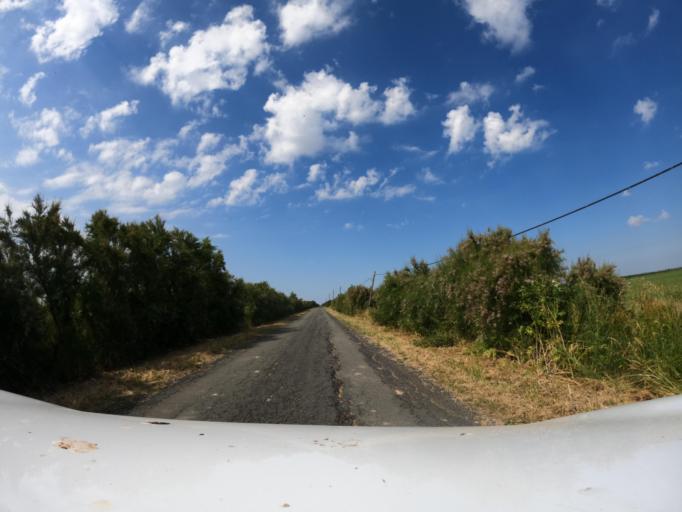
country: FR
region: Poitou-Charentes
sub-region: Departement de la Charente-Maritime
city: Charron
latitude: 46.3327
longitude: -1.1401
